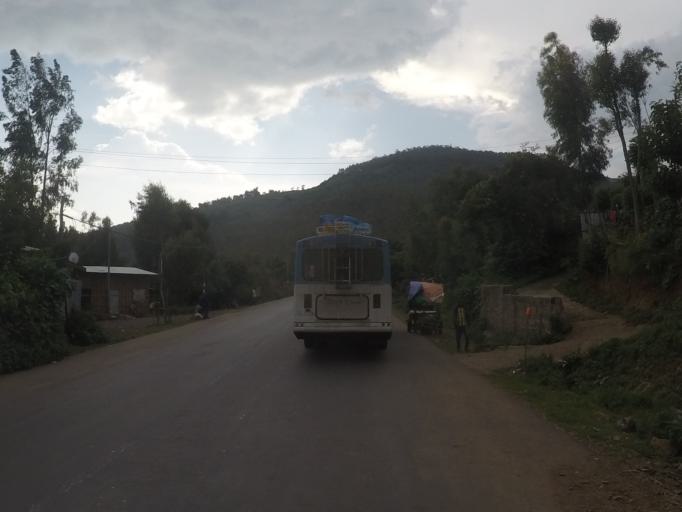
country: ET
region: Amhara
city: Gondar
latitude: 12.6428
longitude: 37.4774
